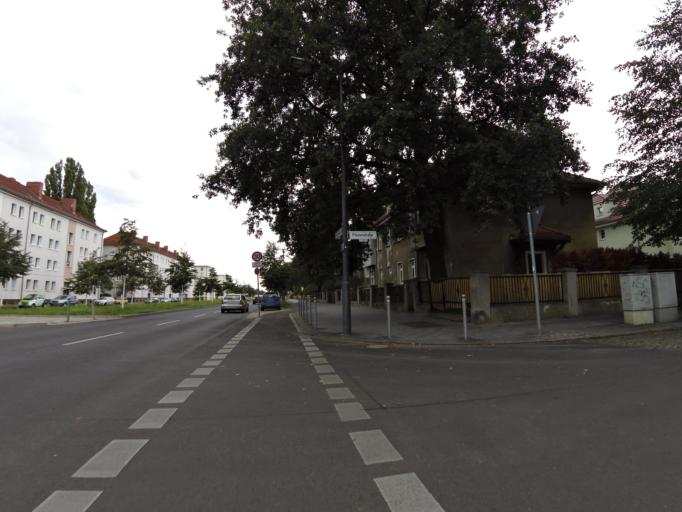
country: DE
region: Berlin
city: Johannisthal
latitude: 52.4476
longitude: 13.5133
